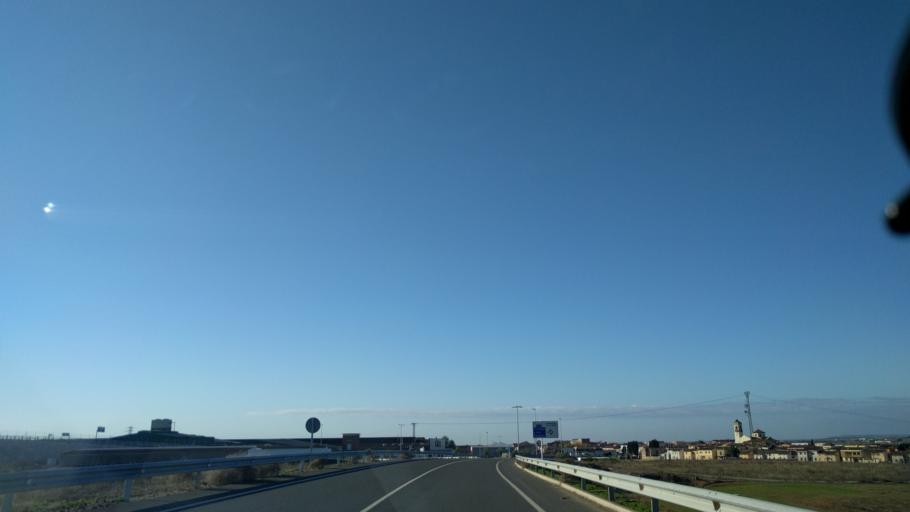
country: ES
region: Catalonia
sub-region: Provincia de Lleida
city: Corbins
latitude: 41.6933
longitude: 0.7356
